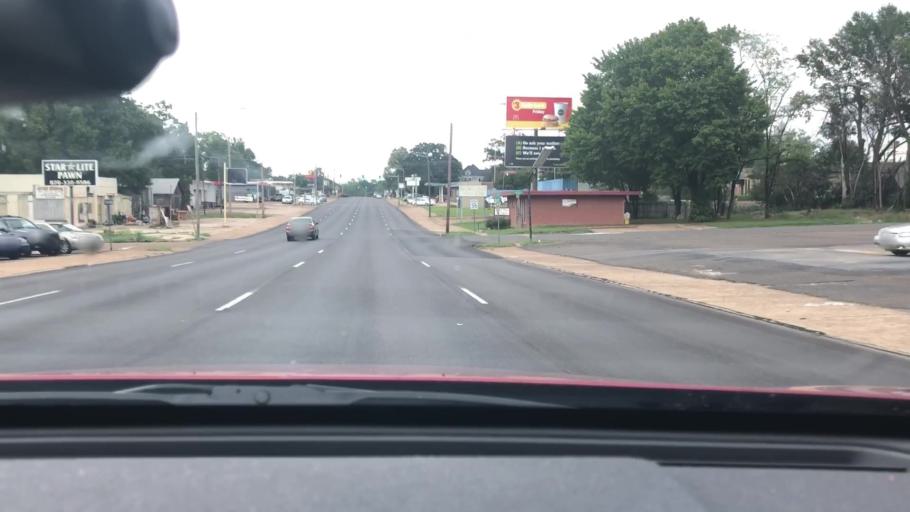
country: US
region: Texas
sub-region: Bowie County
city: Texarkana
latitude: 33.4287
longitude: -94.0399
